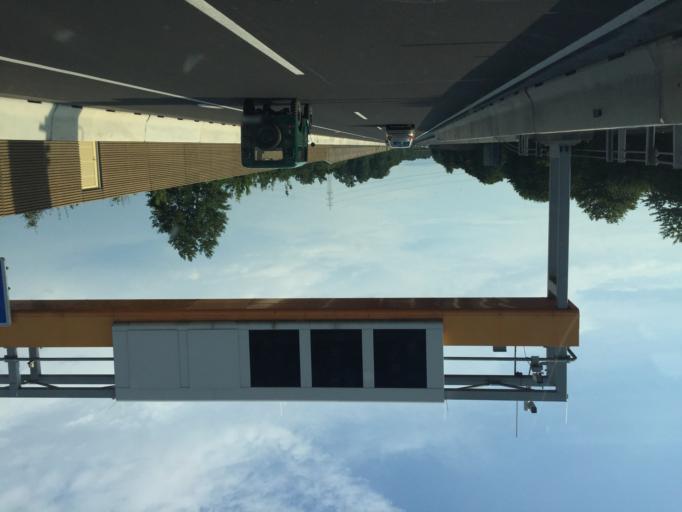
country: AT
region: Styria
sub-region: Politischer Bezirk Leibnitz
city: Weitendorf
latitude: 46.9017
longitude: 15.4723
